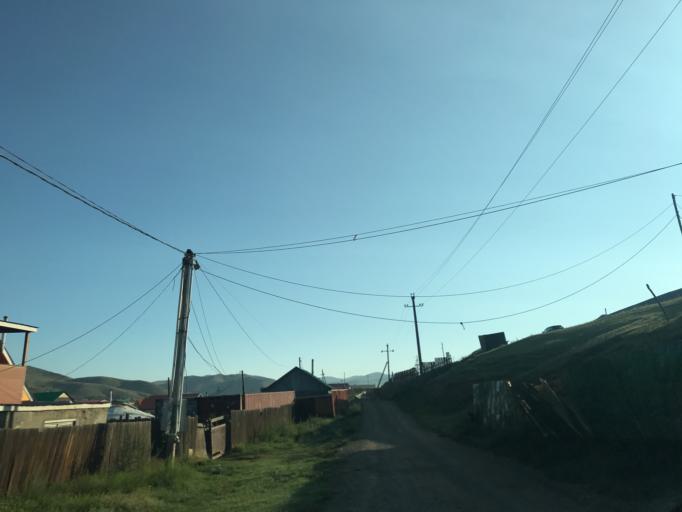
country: MN
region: Ulaanbaatar
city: Ulaanbaatar
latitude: 47.9890
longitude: 106.9638
